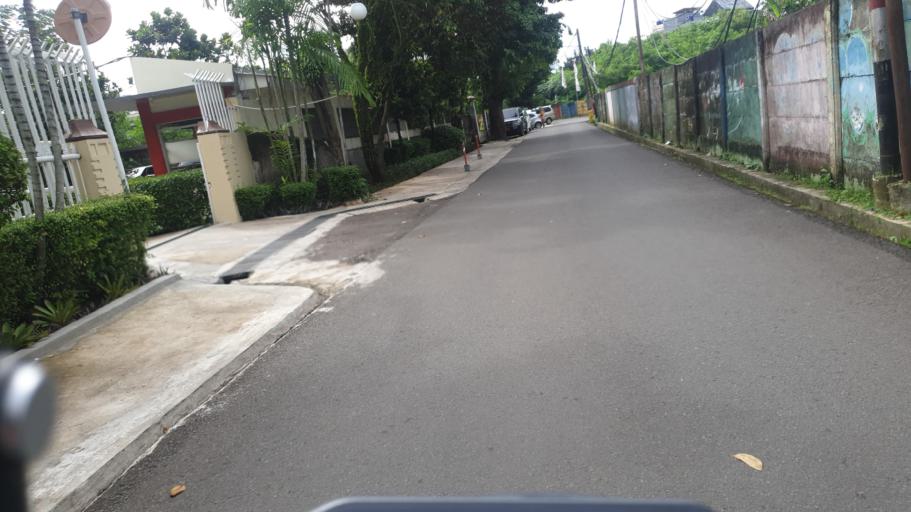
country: ID
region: West Java
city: Pamulang
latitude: -6.2953
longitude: 106.7944
